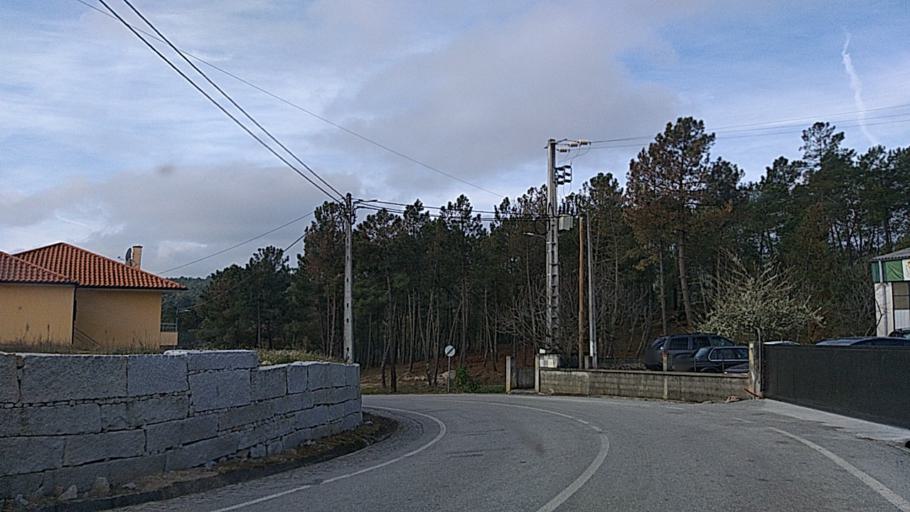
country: PT
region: Guarda
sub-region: Aguiar da Beira
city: Aguiar da Beira
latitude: 40.7290
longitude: -7.5580
